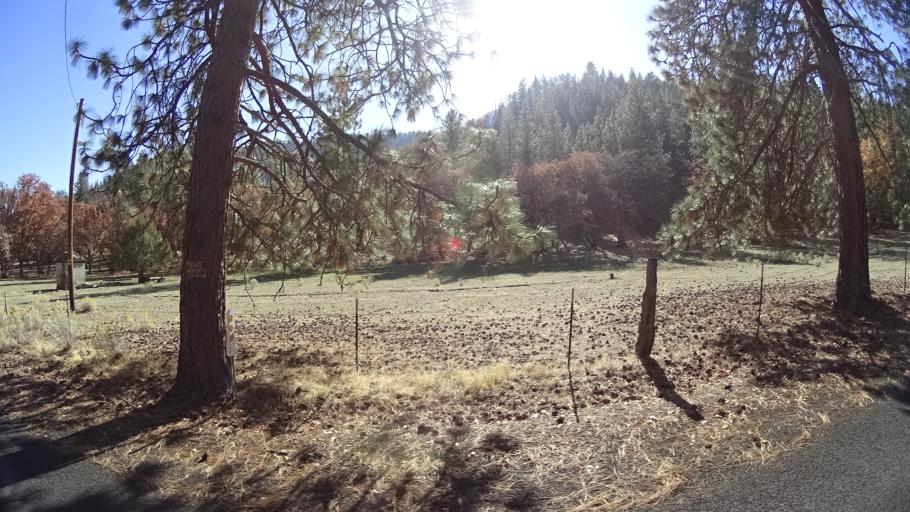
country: US
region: California
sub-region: Siskiyou County
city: Weed
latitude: 41.5036
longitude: -122.5798
